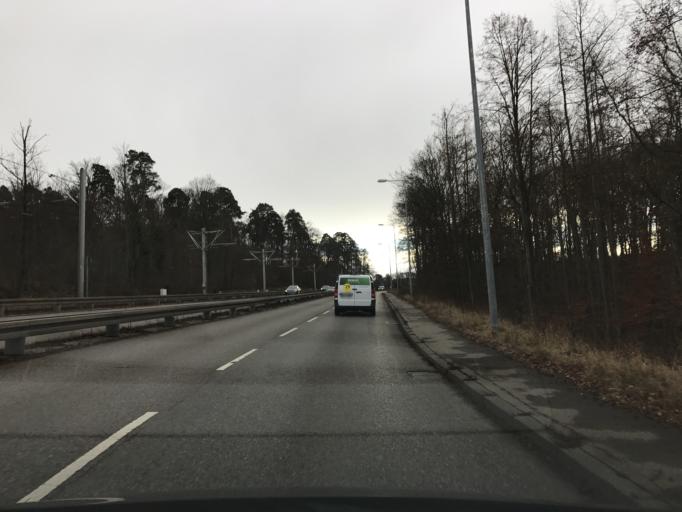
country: DE
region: Baden-Wuerttemberg
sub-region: Regierungsbezirk Stuttgart
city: Stuttgart-Ost
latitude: 48.7656
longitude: 9.2012
